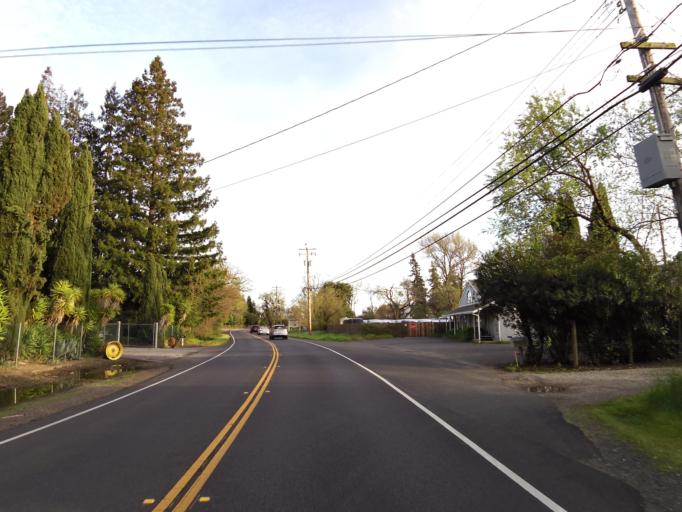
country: US
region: California
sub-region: Sonoma County
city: Sonoma
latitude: 38.2512
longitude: -122.4512
